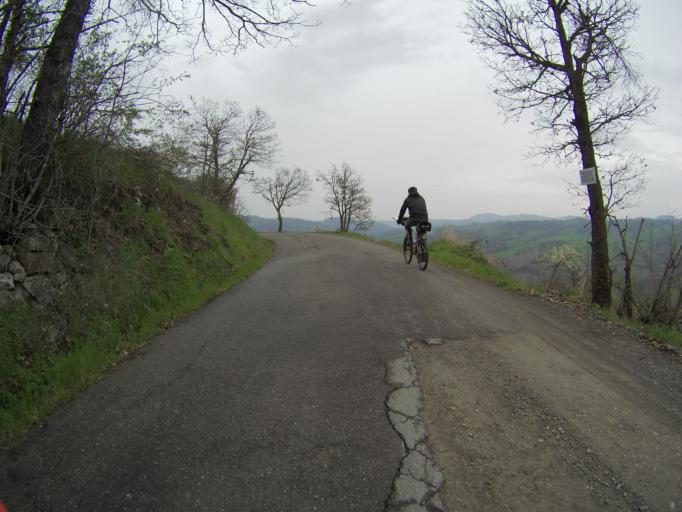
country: IT
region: Emilia-Romagna
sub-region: Provincia di Reggio Emilia
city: Casina
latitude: 44.5359
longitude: 10.4572
